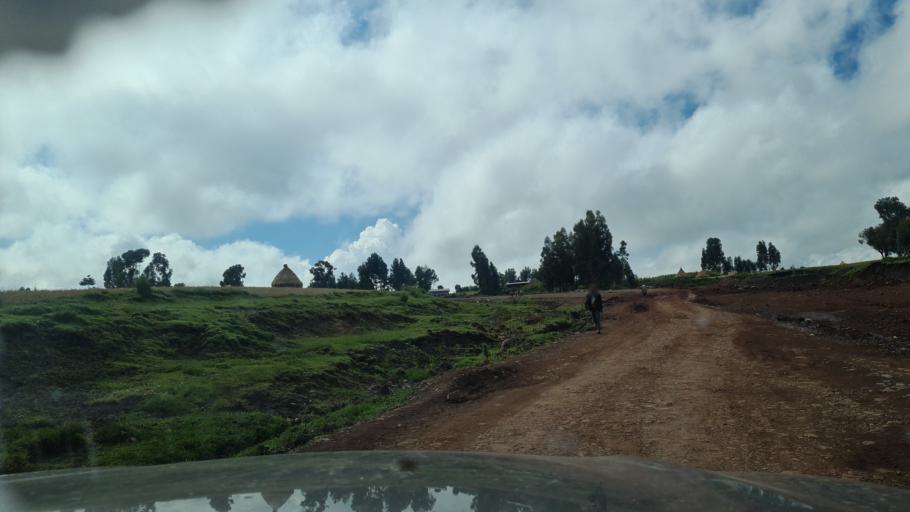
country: ET
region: Oromiya
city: Huruta
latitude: 8.1258
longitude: 39.4362
